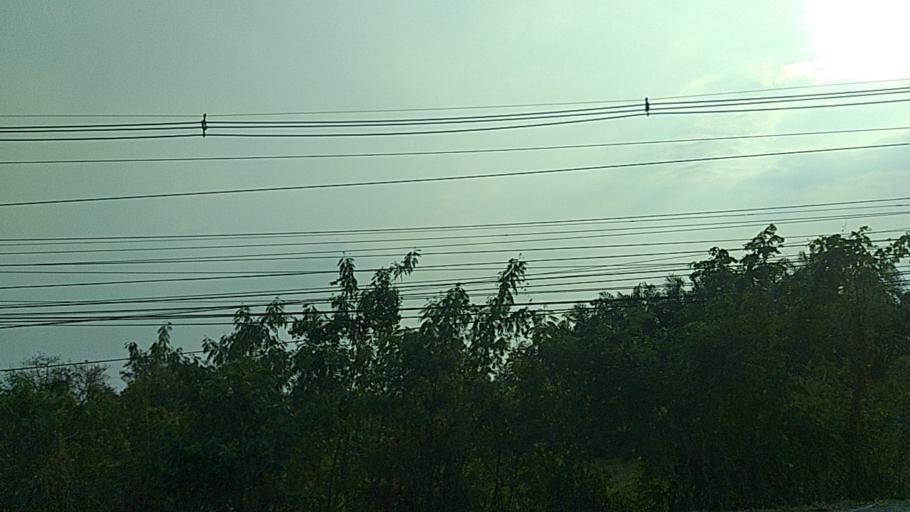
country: TH
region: Nakhon Nayok
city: Nakhon Nayok
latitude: 14.2107
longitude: 101.1780
